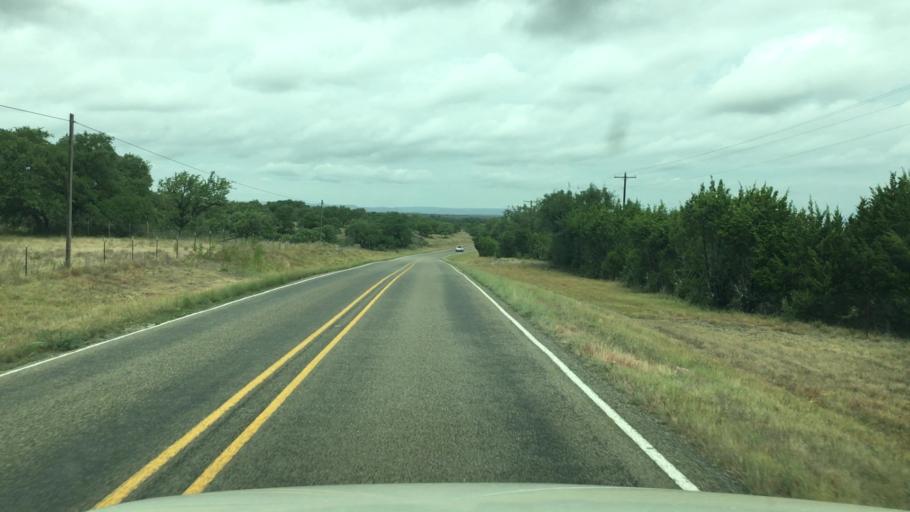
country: US
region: Texas
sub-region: Llano County
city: Horseshoe Bay
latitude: 30.4571
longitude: -98.3970
